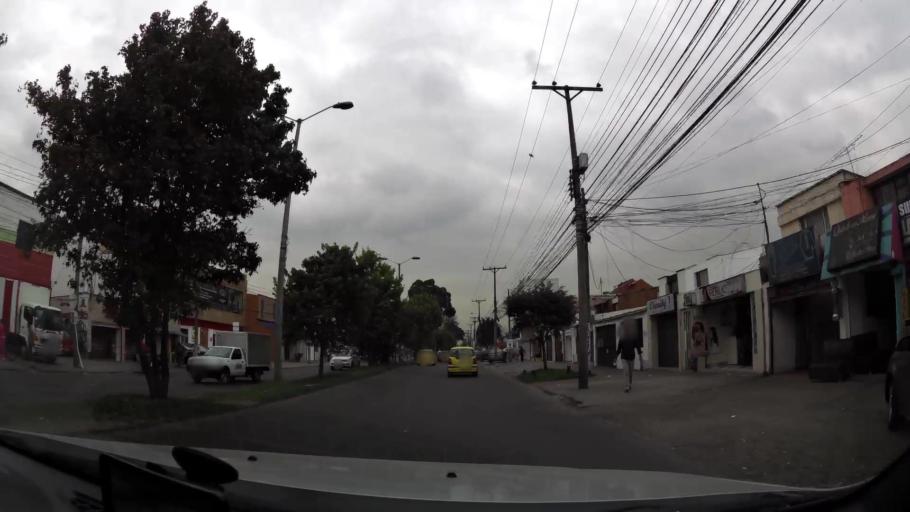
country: CO
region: Bogota D.C.
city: Bogota
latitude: 4.6672
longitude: -74.1208
